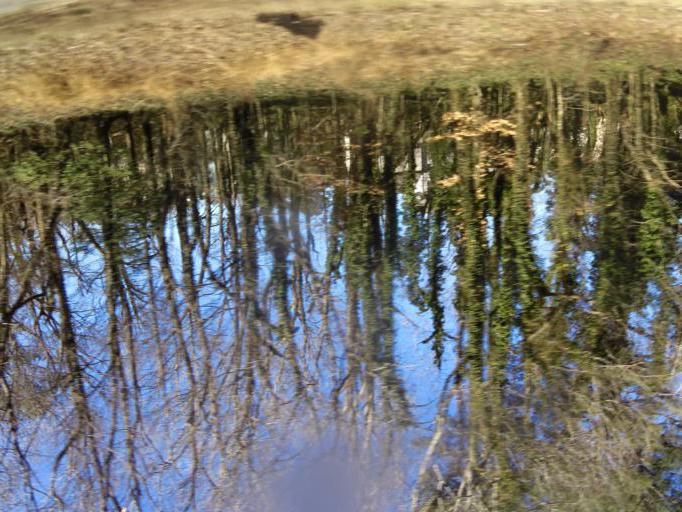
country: US
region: Virginia
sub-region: Isle of Wight County
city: Smithfield
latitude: 36.9762
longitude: -76.6400
